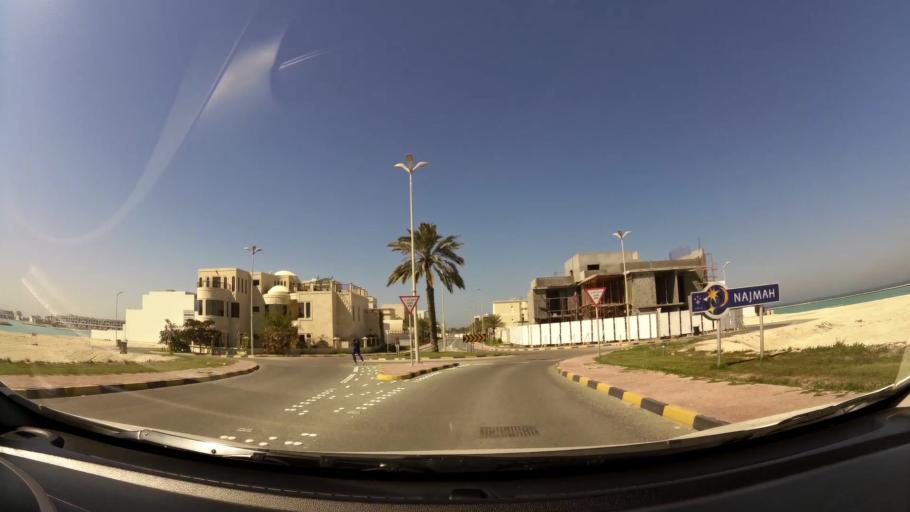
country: BH
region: Muharraq
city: Al Hadd
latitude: 26.2937
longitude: 50.6734
